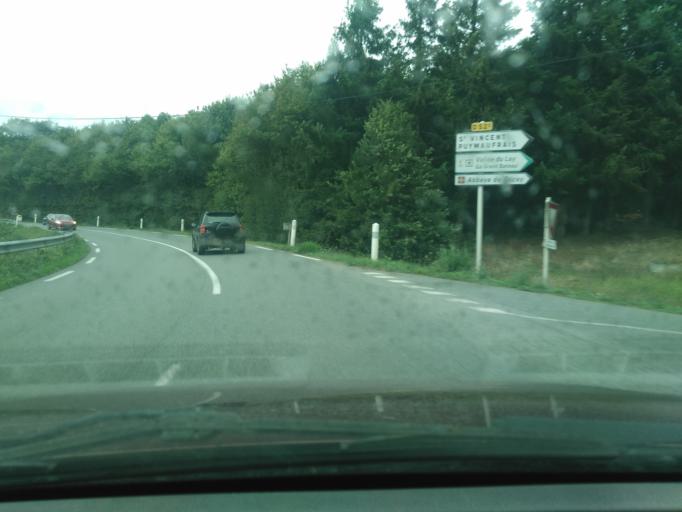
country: FR
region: Pays de la Loire
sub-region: Departement de la Vendee
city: Sainte-Hermine
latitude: 46.5901
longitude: -1.1165
